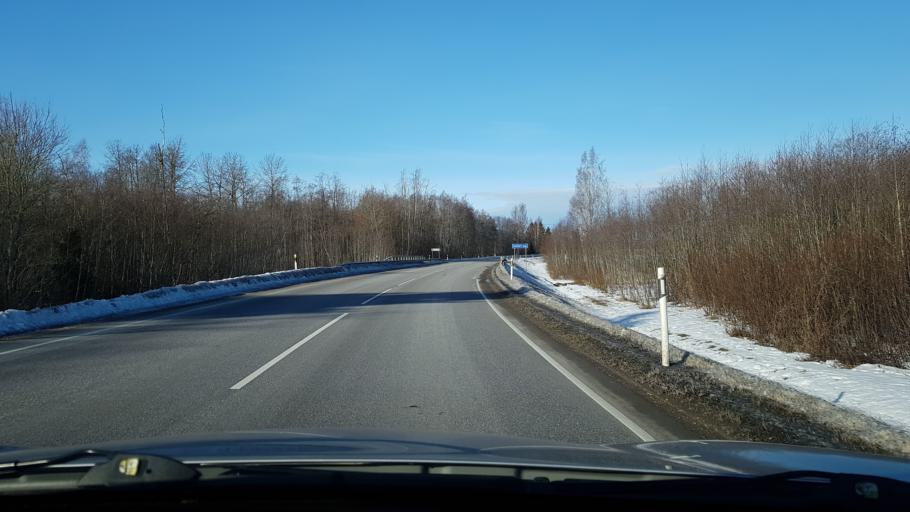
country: EE
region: Jogevamaa
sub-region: Poltsamaa linn
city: Poltsamaa
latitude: 58.6308
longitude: 25.7814
